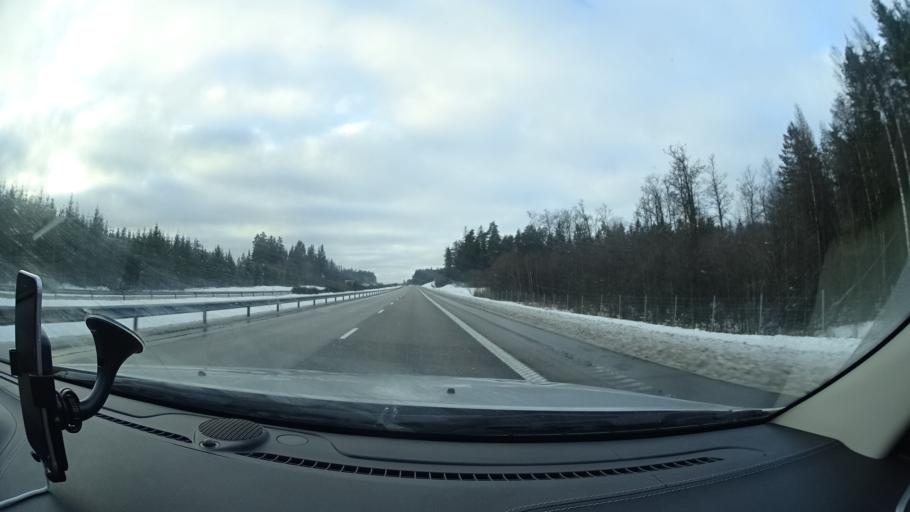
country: SE
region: OEstergoetland
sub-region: Odeshogs Kommun
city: OEdeshoeg
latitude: 58.2453
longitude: 14.7596
